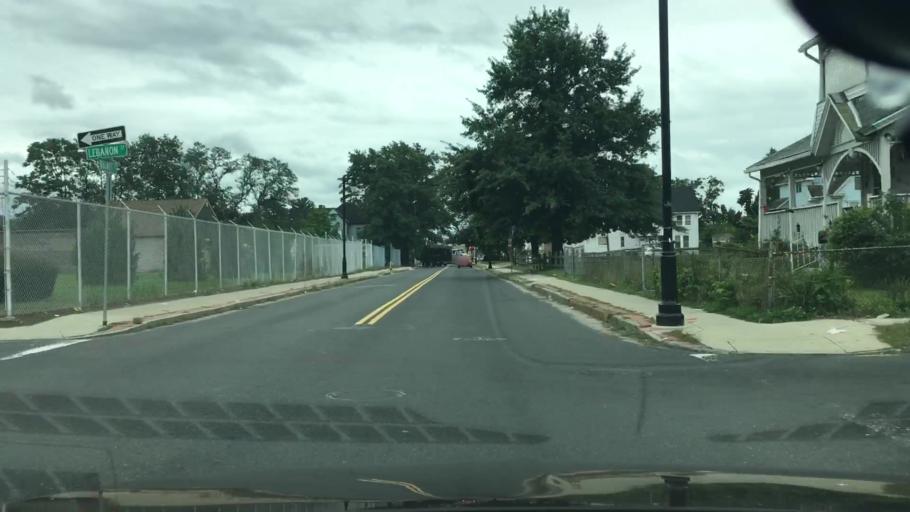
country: US
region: Massachusetts
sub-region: Hampden County
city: Springfield
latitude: 42.1029
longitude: -72.5696
